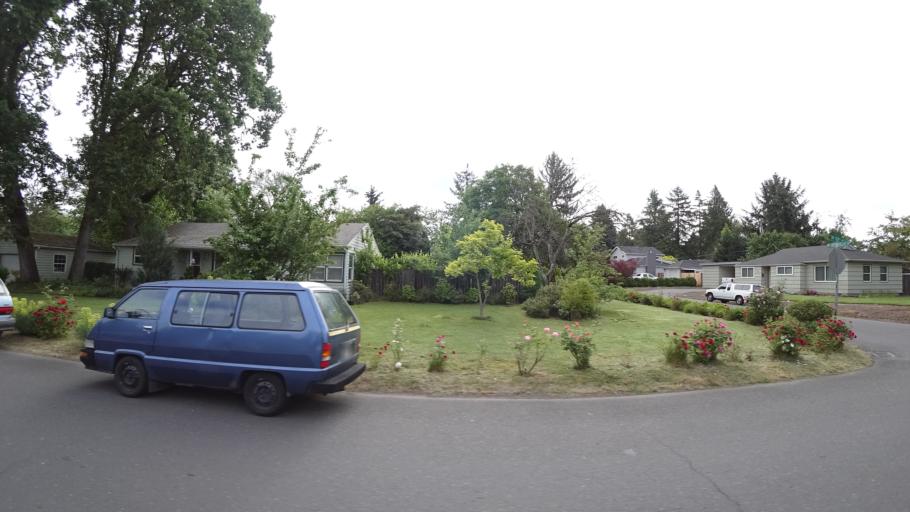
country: US
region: Oregon
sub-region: Washington County
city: Beaverton
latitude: 45.4965
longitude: -122.8045
